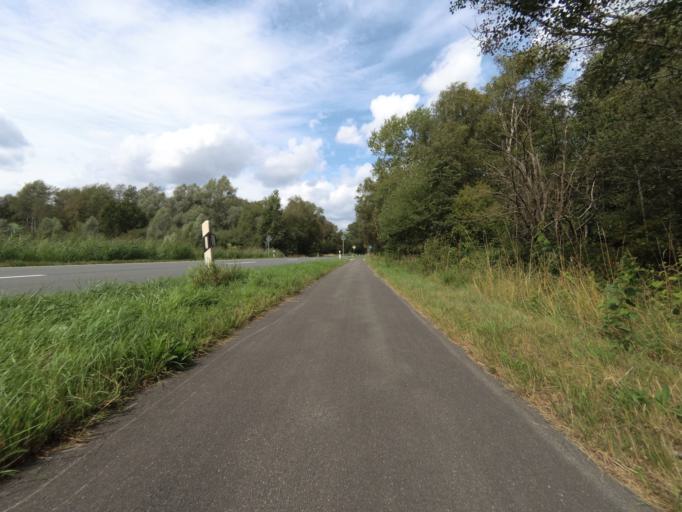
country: DE
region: North Rhine-Westphalia
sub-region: Regierungsbezirk Munster
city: Gronau
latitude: 52.1636
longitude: 6.9802
